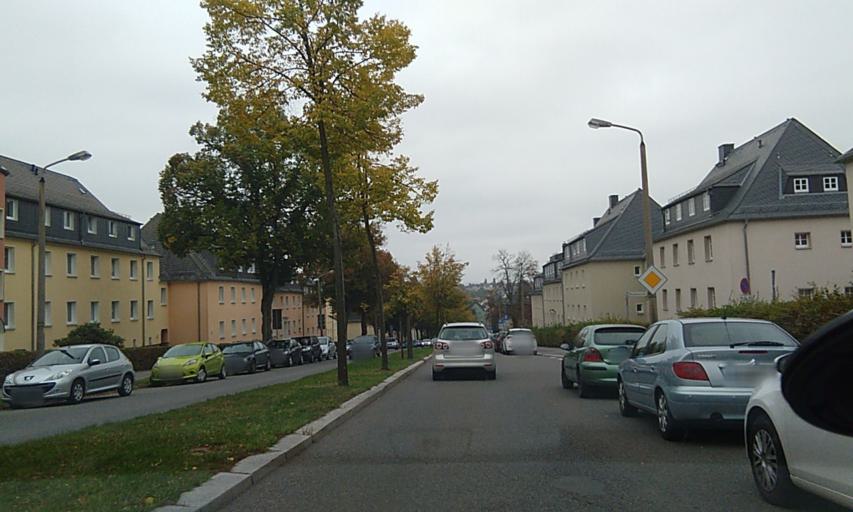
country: DE
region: Saxony
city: Wittgensdorf
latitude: 50.8427
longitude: 12.8860
